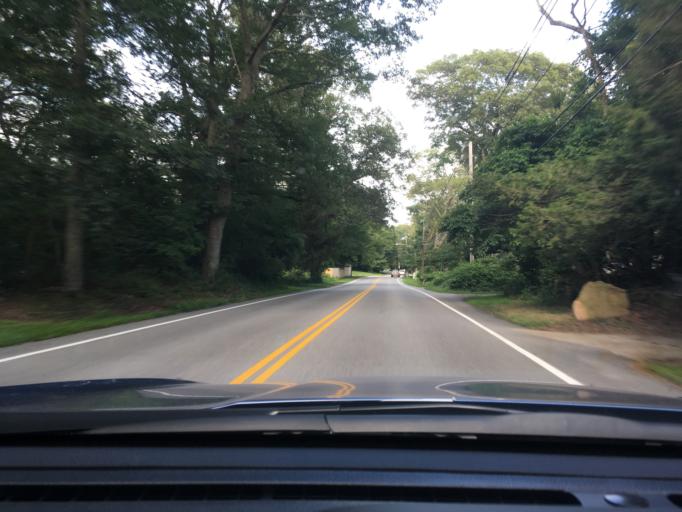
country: US
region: Rhode Island
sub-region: Kent County
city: West Warwick
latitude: 41.6435
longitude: -71.5125
